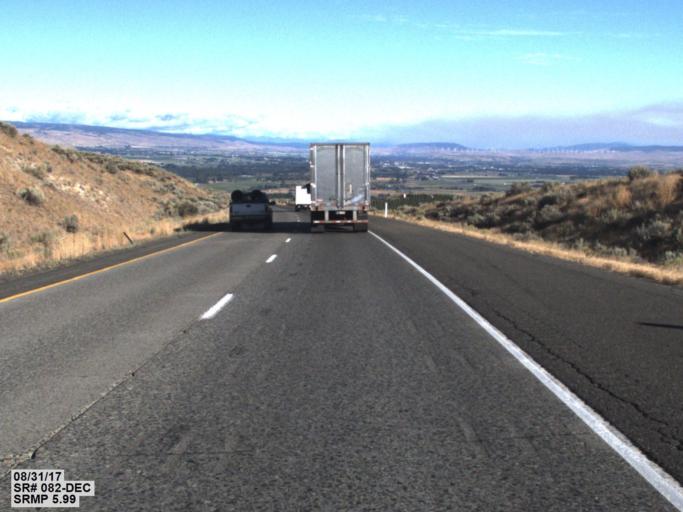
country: US
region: Washington
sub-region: Kittitas County
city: Kittitas
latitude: 46.9018
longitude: -120.4529
